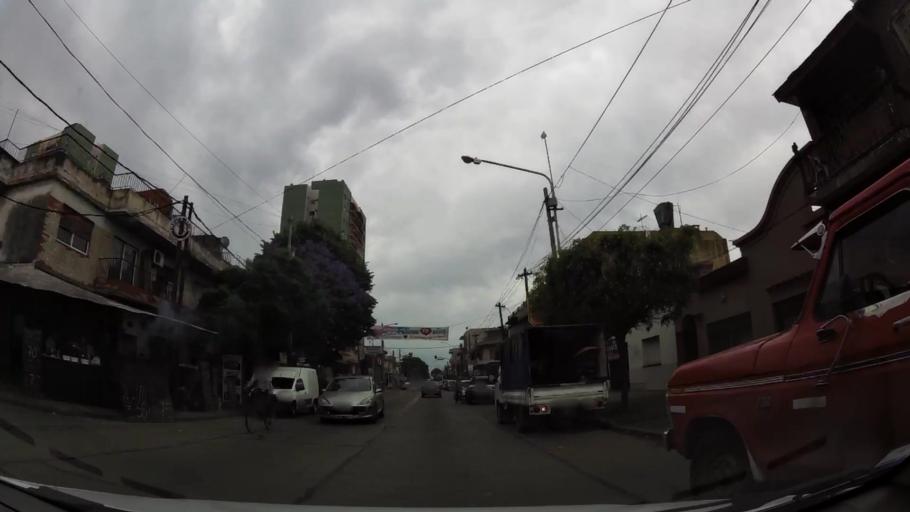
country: AR
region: Buenos Aires
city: San Justo
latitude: -34.6727
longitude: -58.5295
